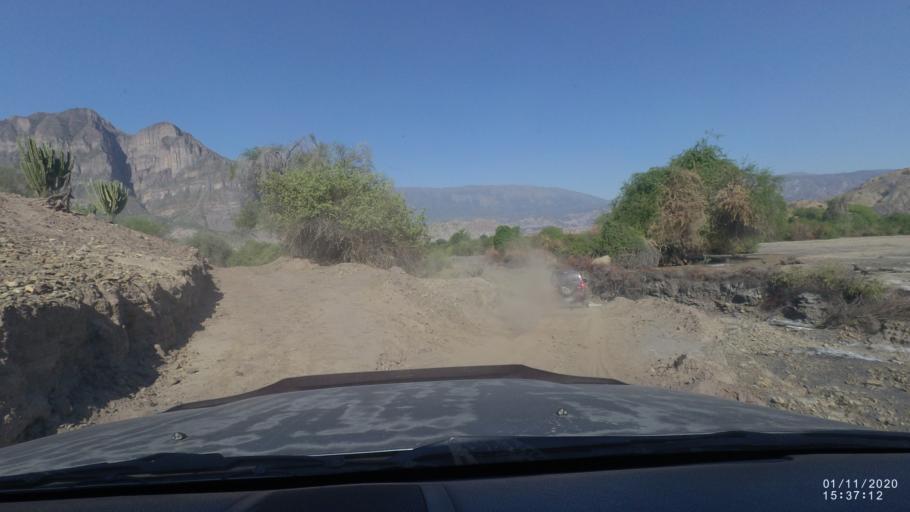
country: BO
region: Chuquisaca
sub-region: Provincia Zudanez
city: Mojocoya
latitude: -18.6759
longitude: -64.5050
